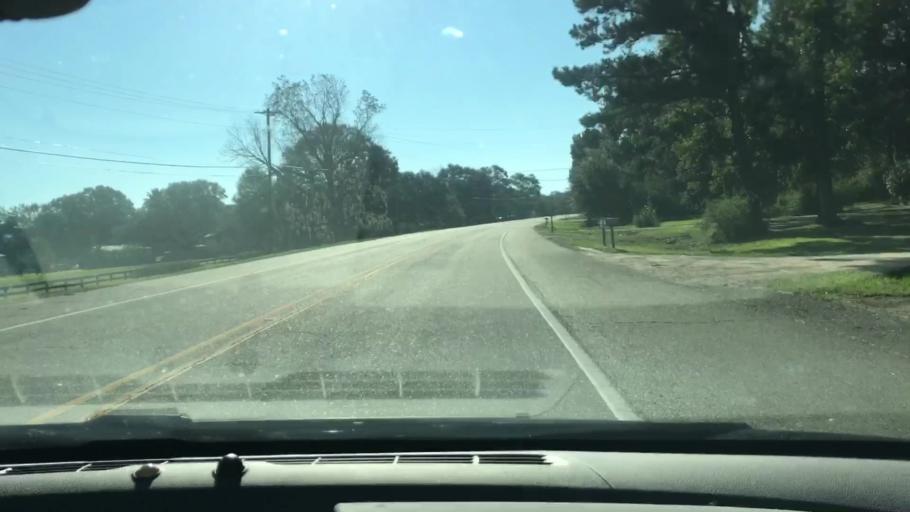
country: US
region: Louisiana
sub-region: Saint Tammany Parish
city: Pearl River
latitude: 30.4585
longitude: -89.8040
